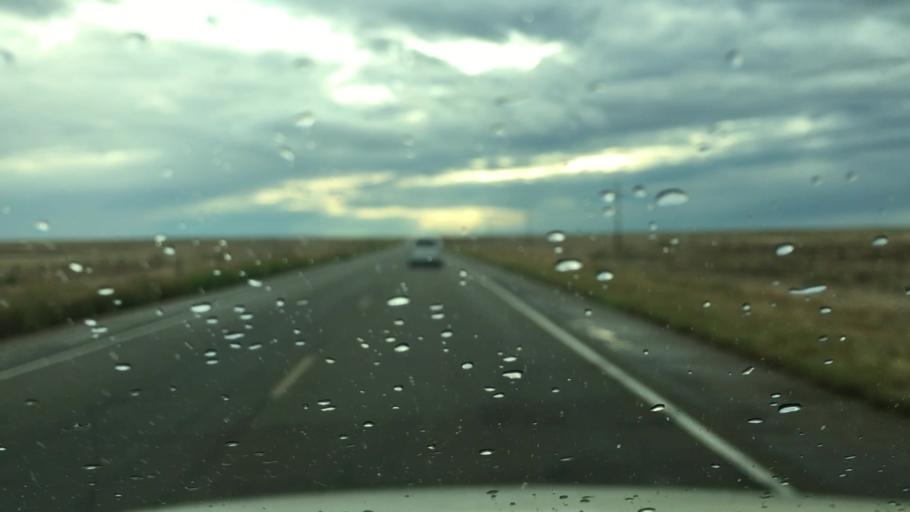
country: US
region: New Mexico
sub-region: Chaves County
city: Roswell
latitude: 33.4047
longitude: -104.3141
